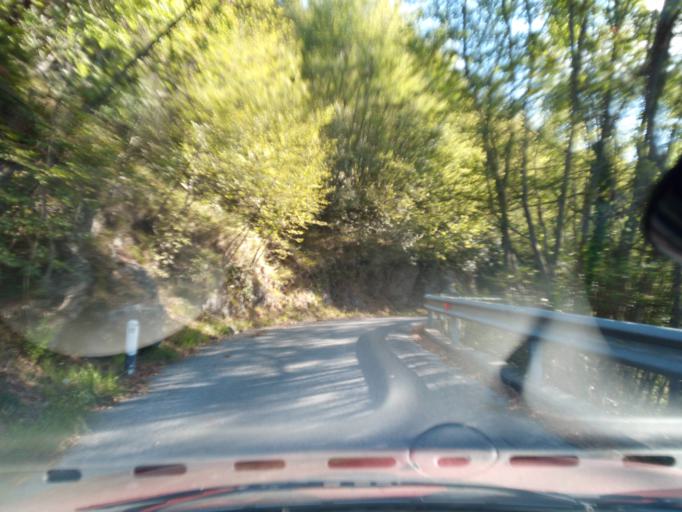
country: IT
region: Liguria
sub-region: Provincia di Genova
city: Isoverde
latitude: 44.4911
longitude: 8.8435
